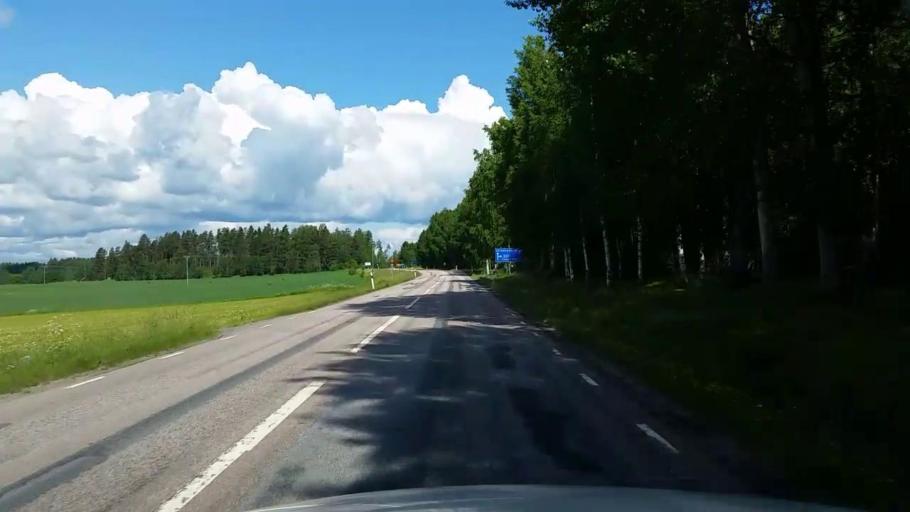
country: SE
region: Vaestmanland
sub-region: Kopings Kommun
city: Kolsva
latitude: 59.6779
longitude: 15.7654
